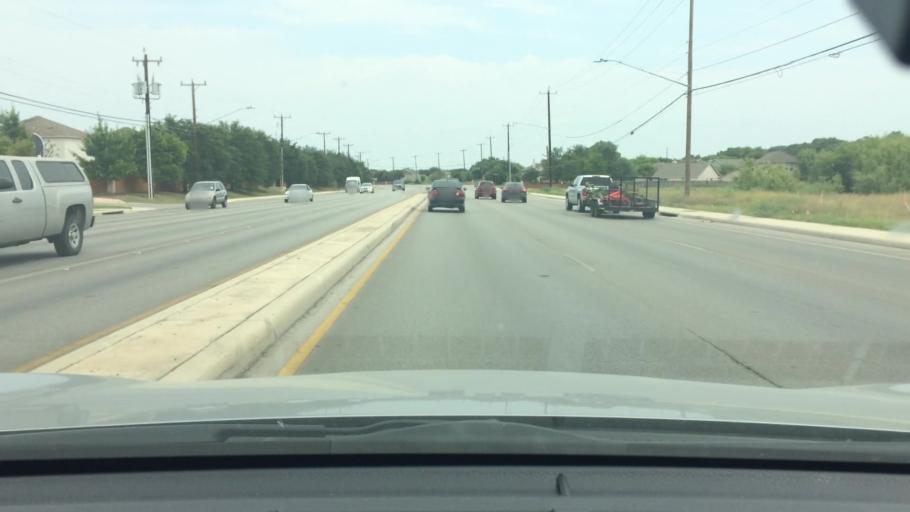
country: US
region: Texas
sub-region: Bexar County
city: Leon Valley
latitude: 29.4778
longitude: -98.6630
